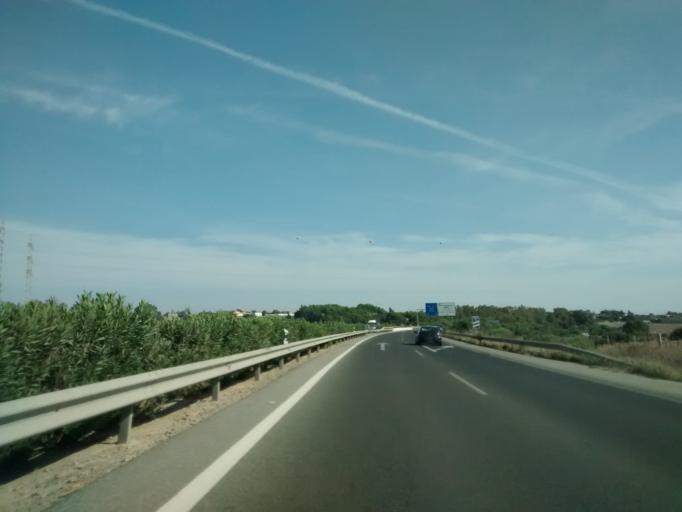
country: ES
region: Andalusia
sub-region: Provincia de Cadiz
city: Chiclana de la Frontera
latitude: 36.4139
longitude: -6.1188
